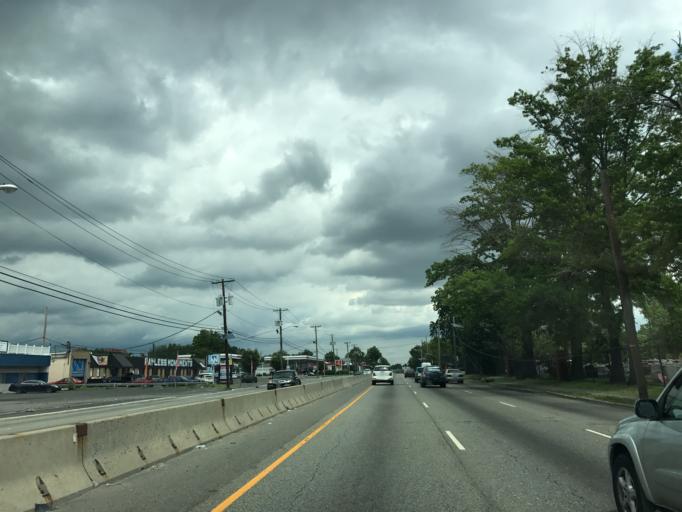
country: US
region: New Jersey
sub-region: Union County
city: Linden
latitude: 40.6306
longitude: -74.2395
